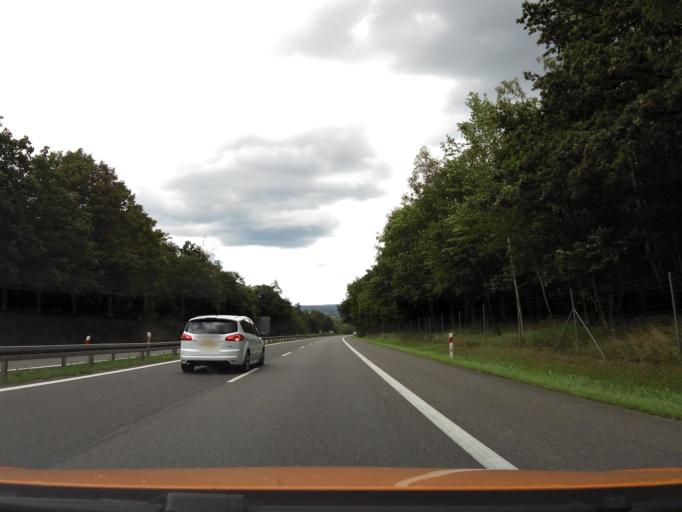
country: PL
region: West Pomeranian Voivodeship
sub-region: Powiat policki
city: Przeclaw
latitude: 53.3415
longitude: 14.4789
